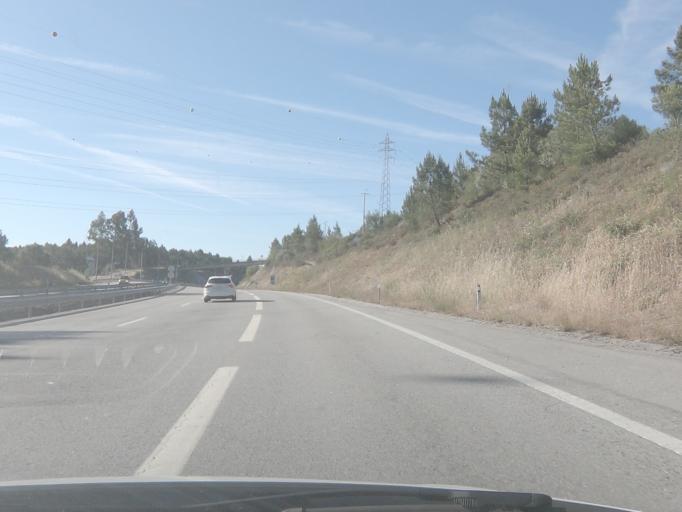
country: PT
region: Viseu
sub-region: Castro Daire
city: Castro Daire
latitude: 40.8150
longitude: -7.9386
